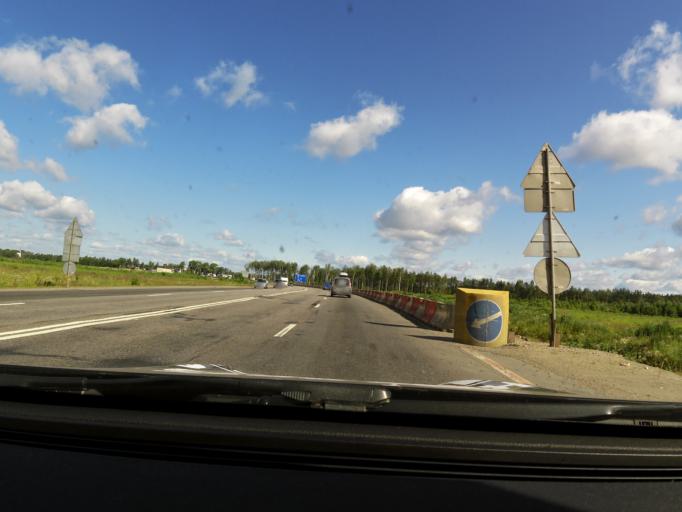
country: RU
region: Tverskaya
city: Tver
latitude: 56.8801
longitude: 35.7838
